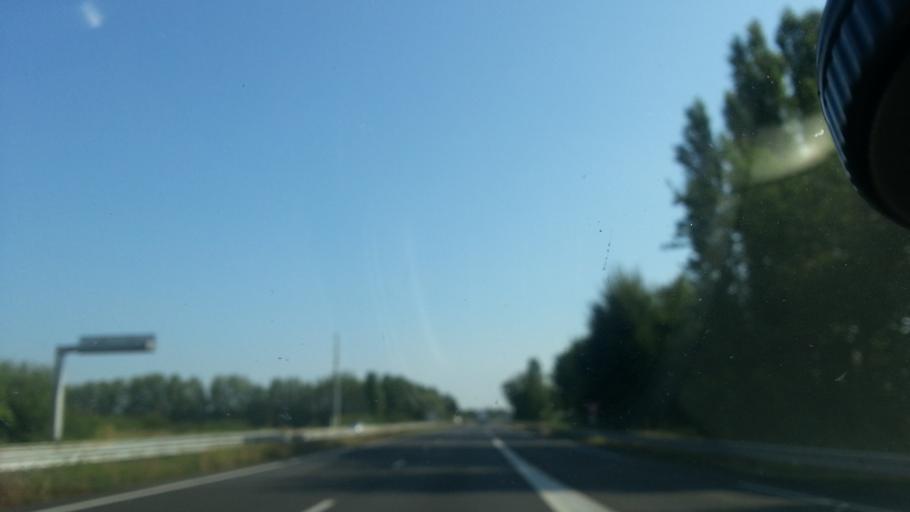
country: FR
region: Centre
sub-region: Departement d'Indre-et-Loire
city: La Celle-Saint-Avant
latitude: 47.0282
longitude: 0.5688
